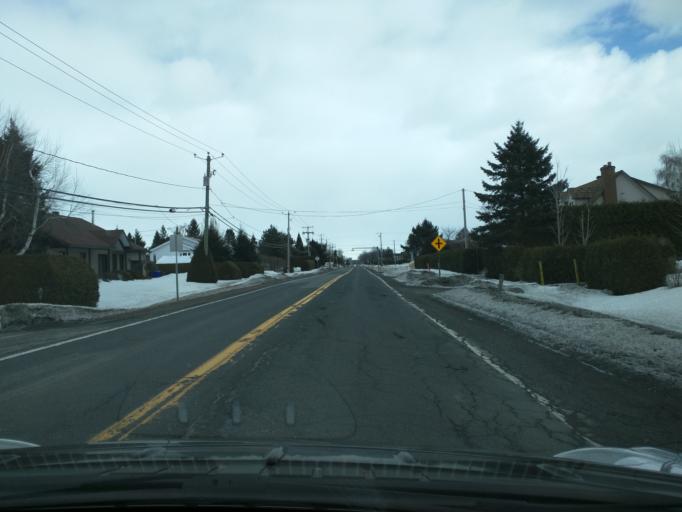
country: CA
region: Quebec
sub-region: Monteregie
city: Sainte-Julie
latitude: 45.6669
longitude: -73.2838
